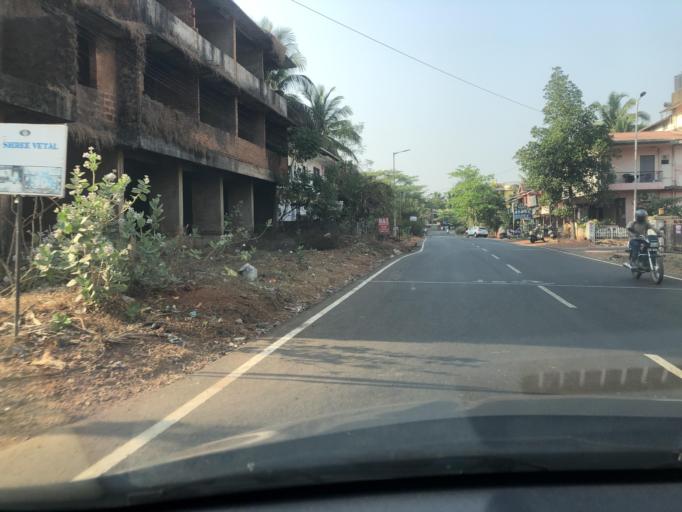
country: IN
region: Goa
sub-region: North Goa
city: Serula
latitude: 15.5278
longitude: 73.8294
